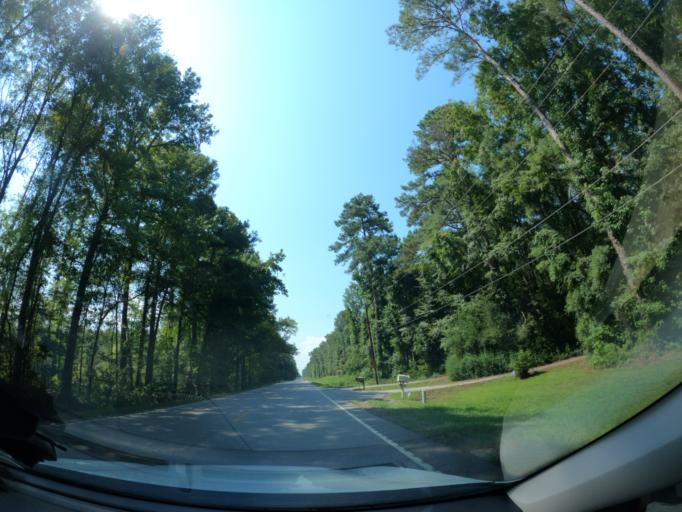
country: US
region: South Carolina
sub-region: Richland County
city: Hopkins
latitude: 33.9112
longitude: -80.9396
